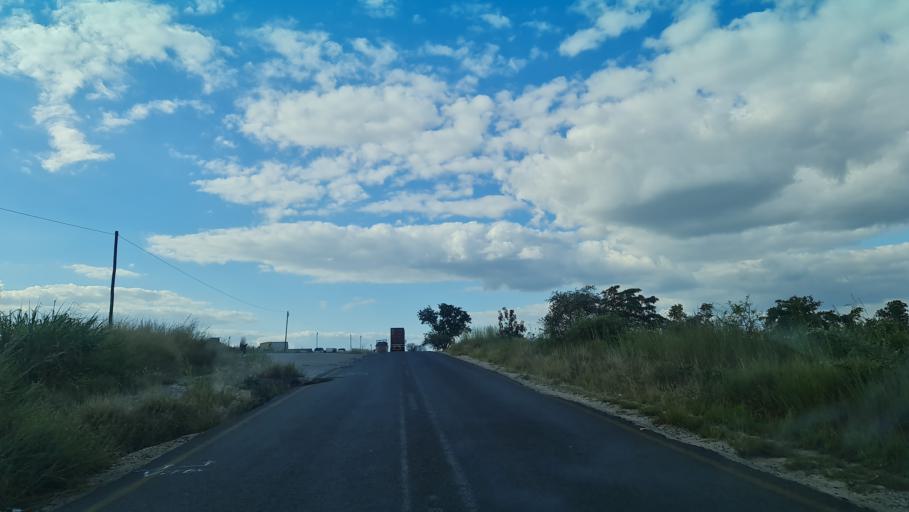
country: MZ
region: Manica
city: Chimoio
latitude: -19.2214
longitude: 33.9211
